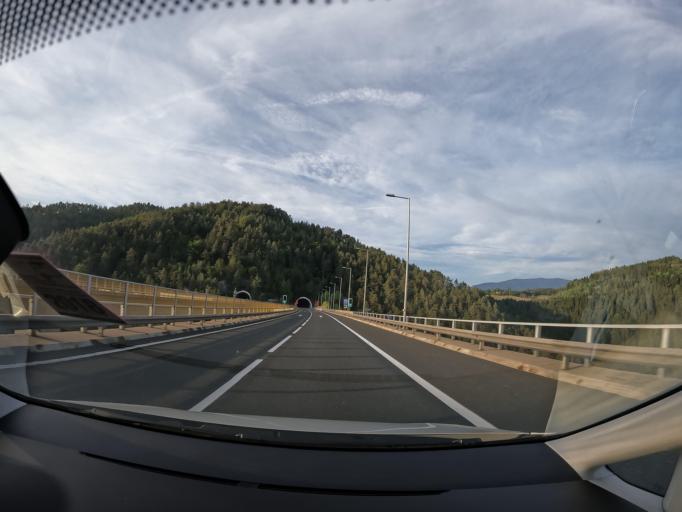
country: AT
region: Carinthia
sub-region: Politischer Bezirk Wolfsberg
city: Sankt Andrae
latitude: 46.7244
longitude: 14.7994
